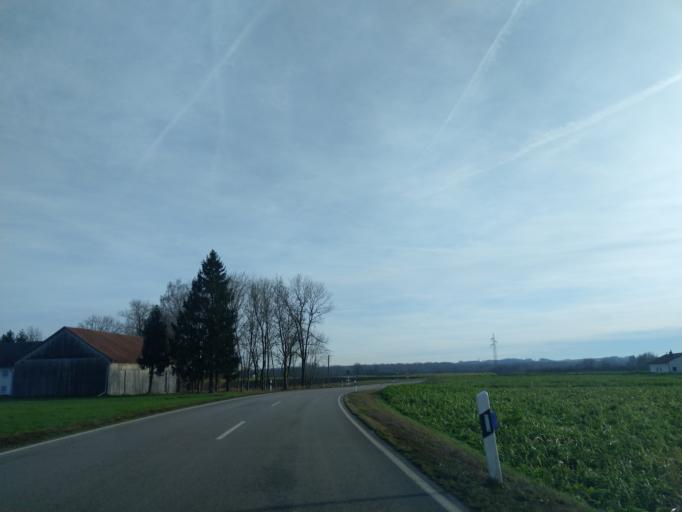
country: DE
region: Bavaria
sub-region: Lower Bavaria
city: Oberporing
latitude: 48.7190
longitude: 12.7970
